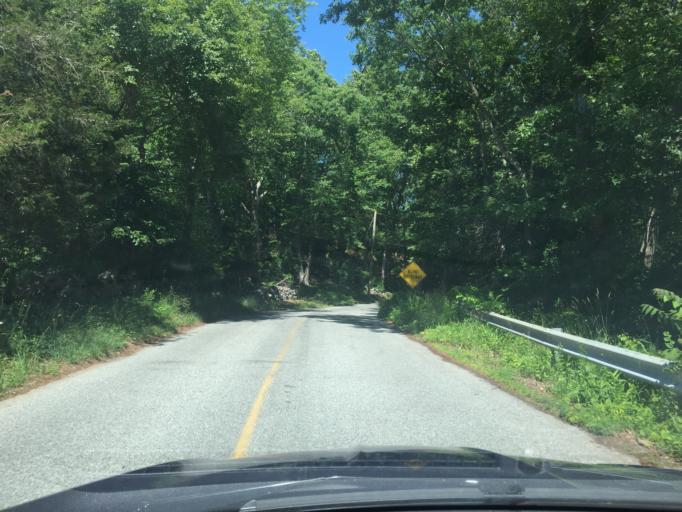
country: US
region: Connecticut
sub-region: New London County
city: Pawcatuck
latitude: 41.4430
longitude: -71.8803
